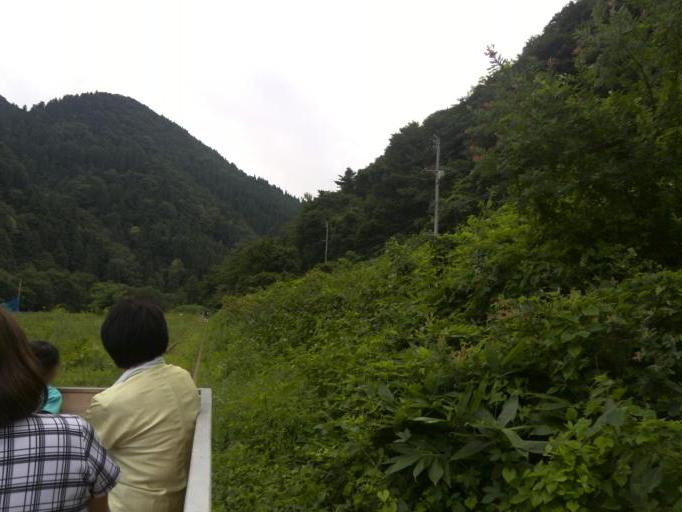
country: JP
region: Akita
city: Odate
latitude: 40.2941
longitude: 140.6367
